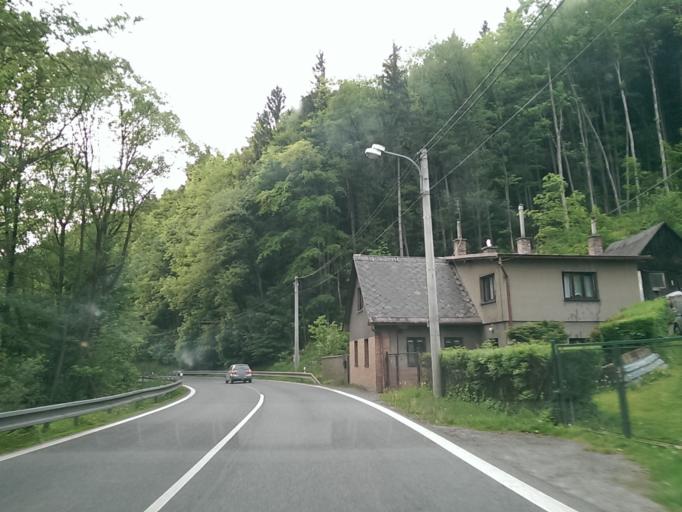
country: CZ
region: Liberecky
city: Zelezny Brod
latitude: 50.6434
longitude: 15.2373
